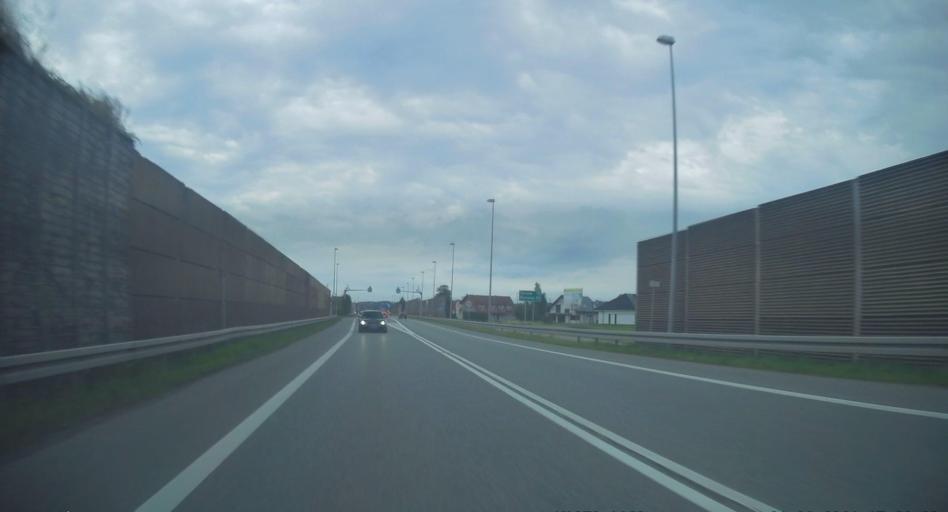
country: PL
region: Lesser Poland Voivodeship
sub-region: Powiat tarnowski
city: Wojnicz
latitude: 49.9641
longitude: 20.8570
